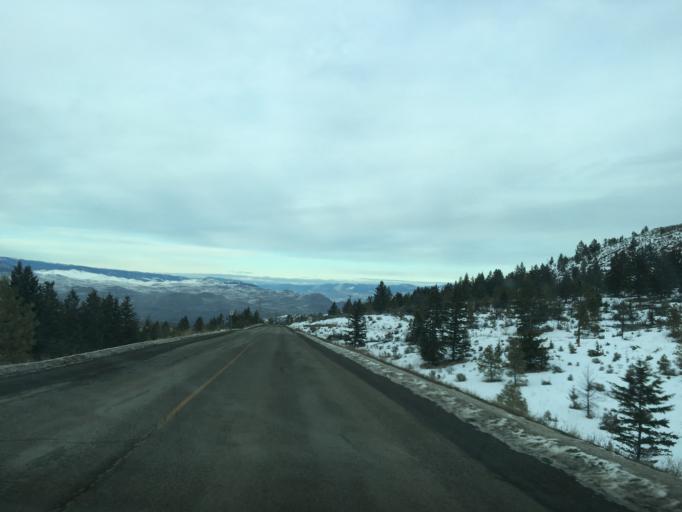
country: CA
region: British Columbia
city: Kamloops
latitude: 50.6516
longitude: -120.4524
